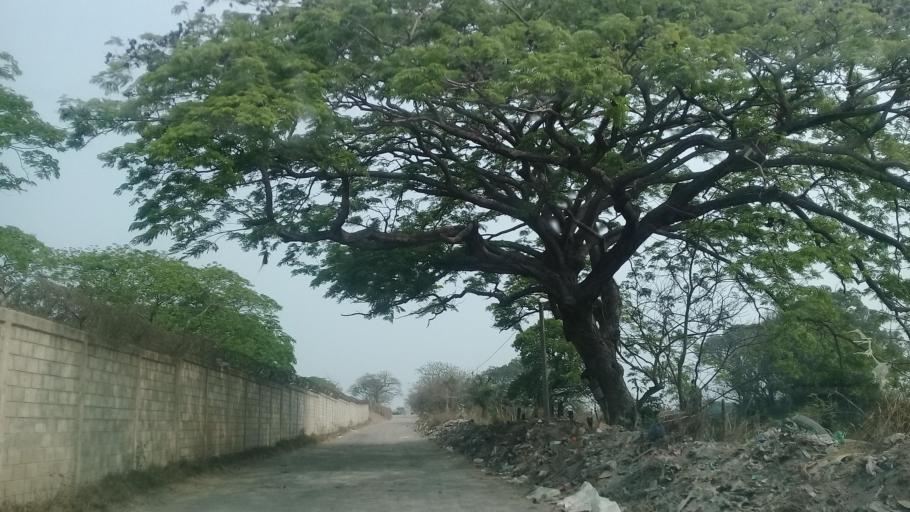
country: MX
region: Veracruz
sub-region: Veracruz
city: Lomas de Rio Medio Cuatro
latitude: 19.1896
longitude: -96.2225
